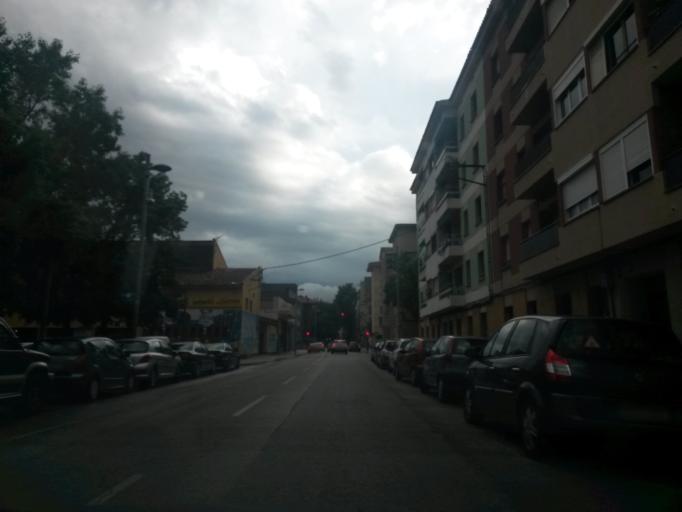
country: ES
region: Catalonia
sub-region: Provincia de Girona
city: Girona
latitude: 41.9716
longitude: 2.8121
